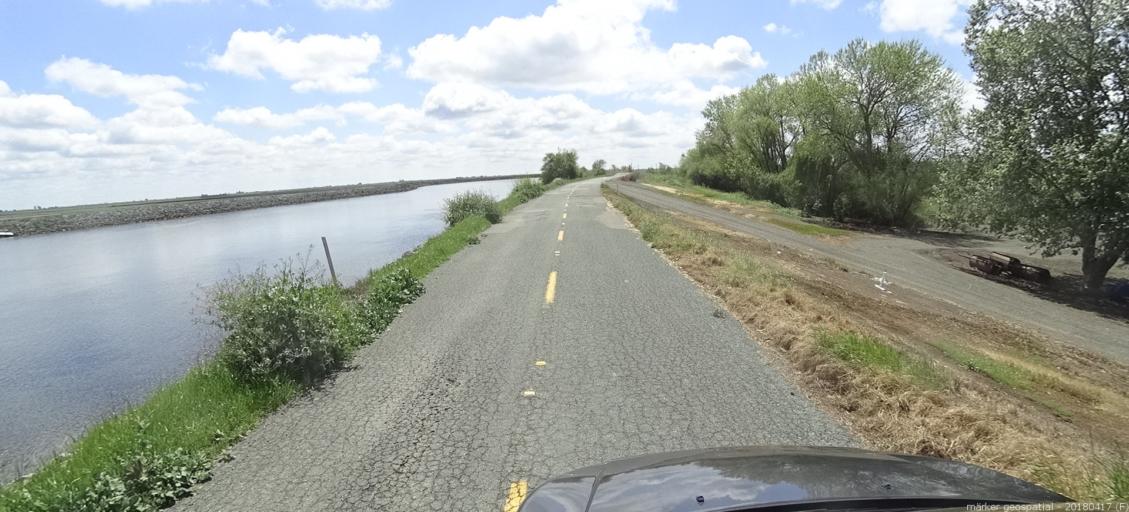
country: US
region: California
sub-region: Sacramento County
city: Walnut Grove
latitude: 38.1892
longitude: -121.5273
